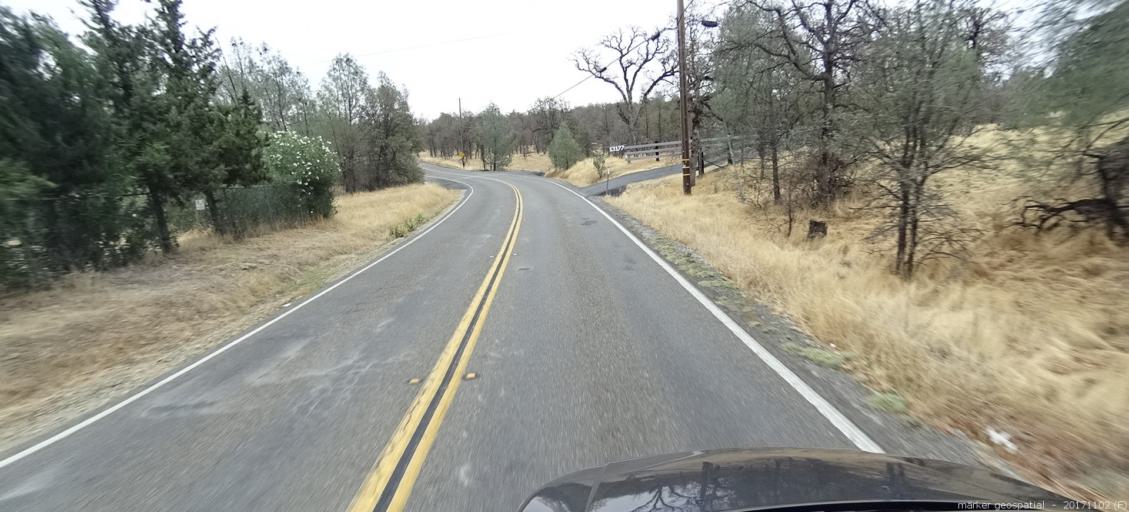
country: US
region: California
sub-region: Shasta County
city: Shasta Lake
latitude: 40.6705
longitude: -122.3124
